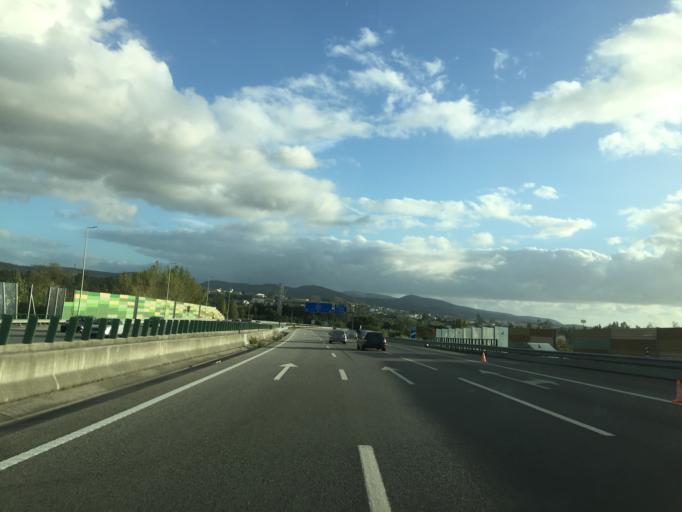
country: PT
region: Coimbra
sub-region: Condeixa-A-Nova
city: Condeixa-a-Nova
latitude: 40.1362
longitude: -8.4961
